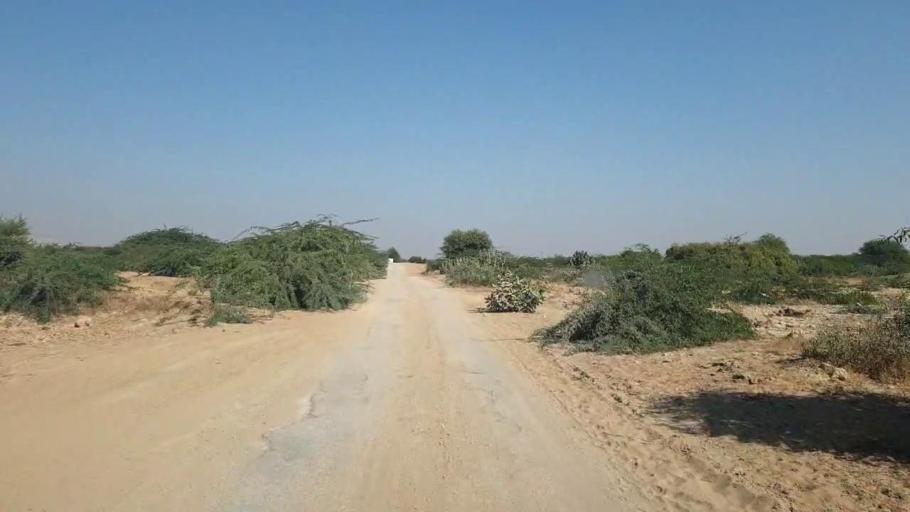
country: PK
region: Sindh
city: Gharo
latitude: 25.1775
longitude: 67.7341
